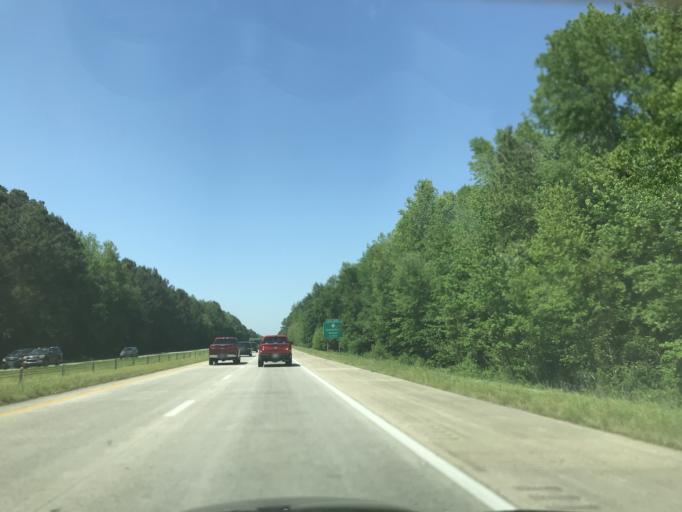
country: US
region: North Carolina
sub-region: Johnston County
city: Benson
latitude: 35.4836
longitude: -78.5511
